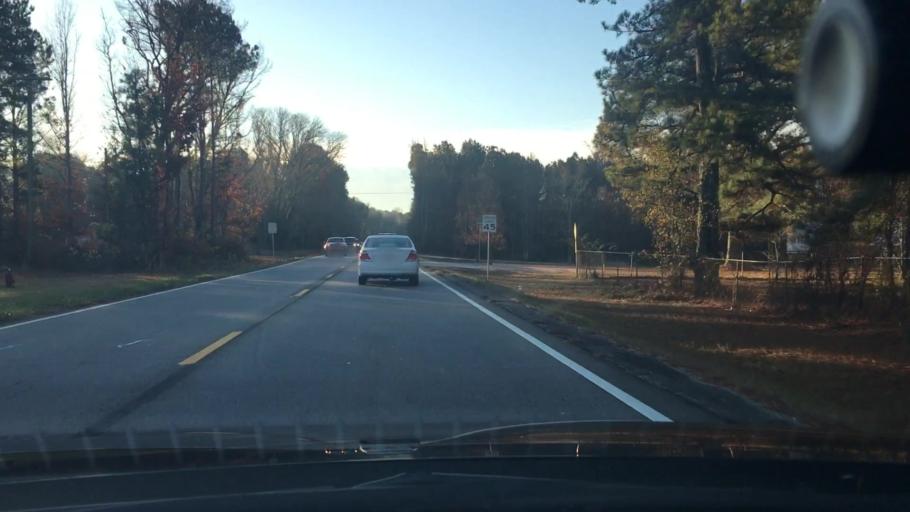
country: US
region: Georgia
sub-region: Fayette County
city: Peachtree City
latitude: 33.3559
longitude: -84.6599
